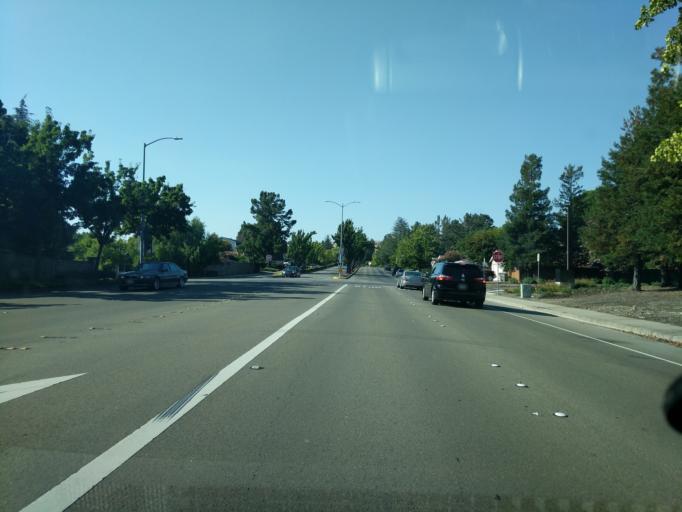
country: US
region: California
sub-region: Alameda County
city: Dublin
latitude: 37.7340
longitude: -121.9244
